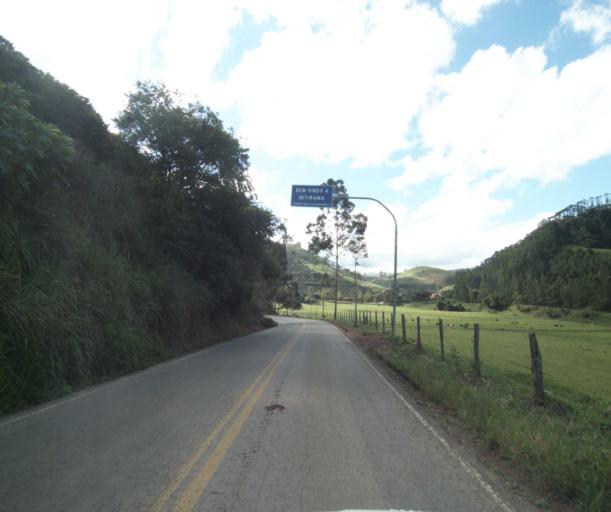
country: BR
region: Espirito Santo
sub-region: Irupi
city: Irupi
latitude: -20.5403
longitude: -41.6553
